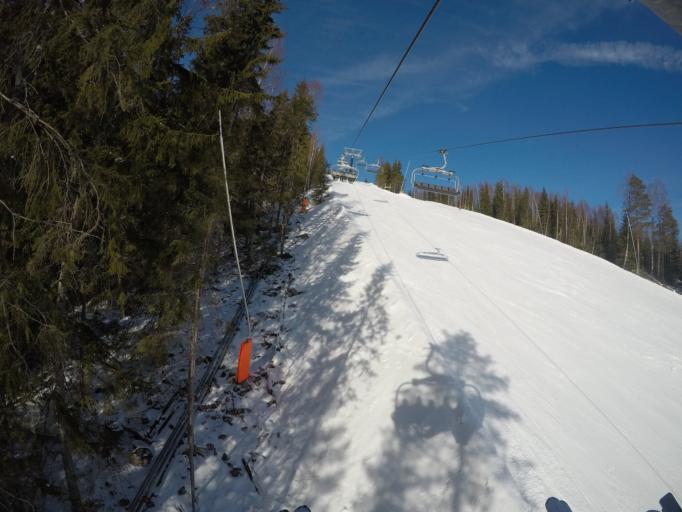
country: SE
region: Dalarna
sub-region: Borlange Kommun
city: Borlaenge
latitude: 60.3793
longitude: 15.4021
